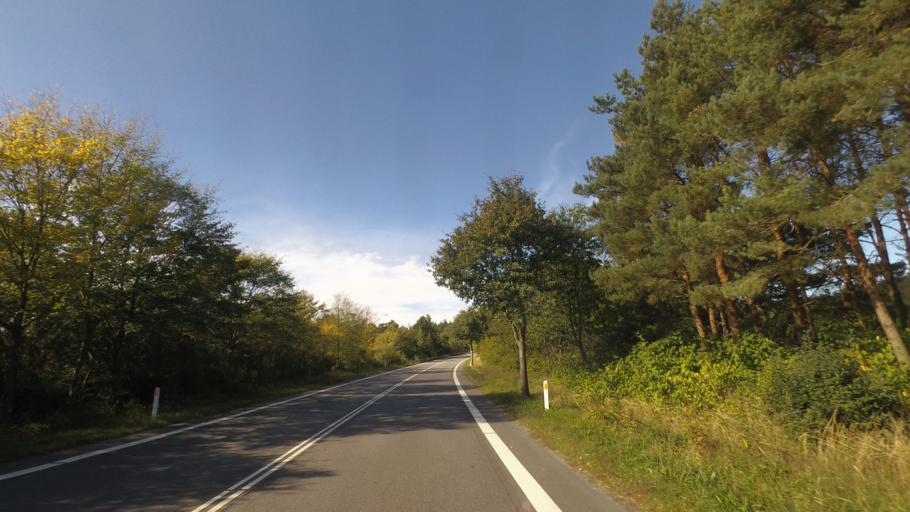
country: DK
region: Capital Region
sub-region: Bornholm Kommune
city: Ronne
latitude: 55.0807
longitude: 14.7551
